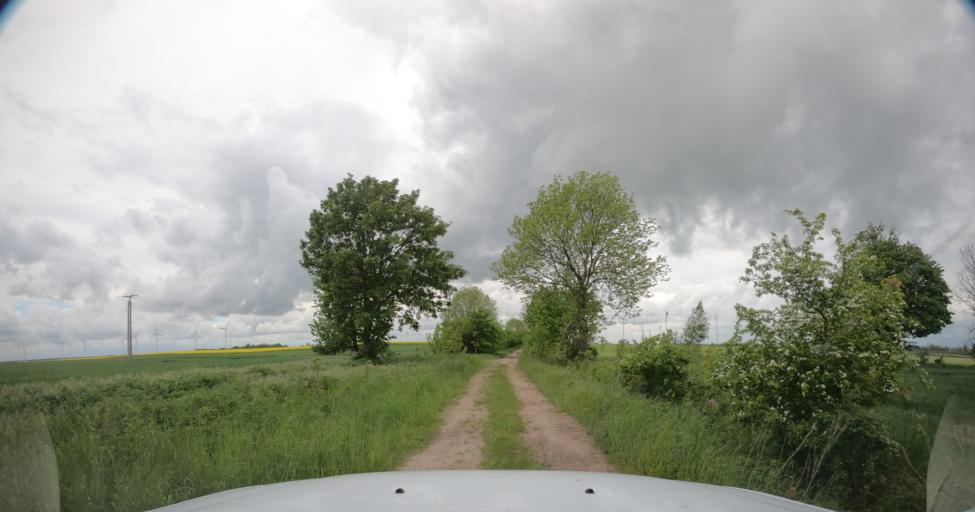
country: PL
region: West Pomeranian Voivodeship
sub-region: Powiat pyrzycki
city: Kozielice
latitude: 53.0894
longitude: 14.8220
